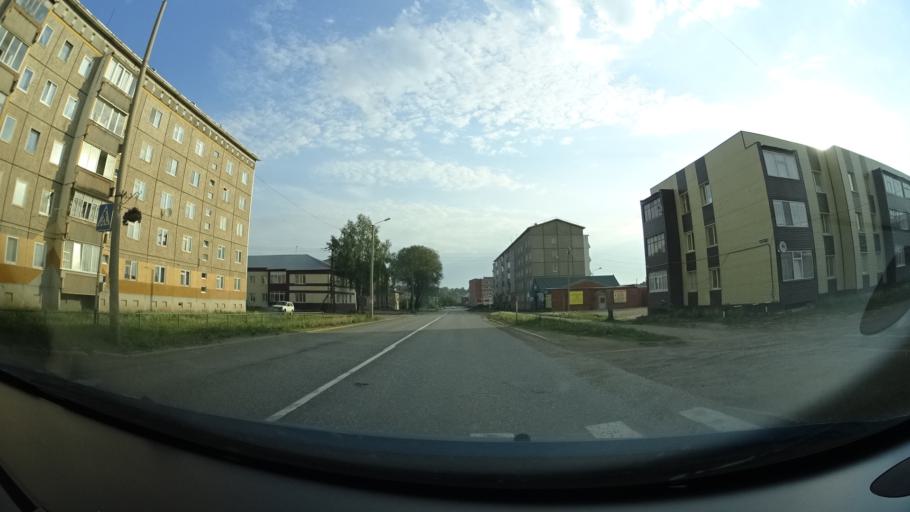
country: RU
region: Perm
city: Barda
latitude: 56.9285
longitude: 55.5924
